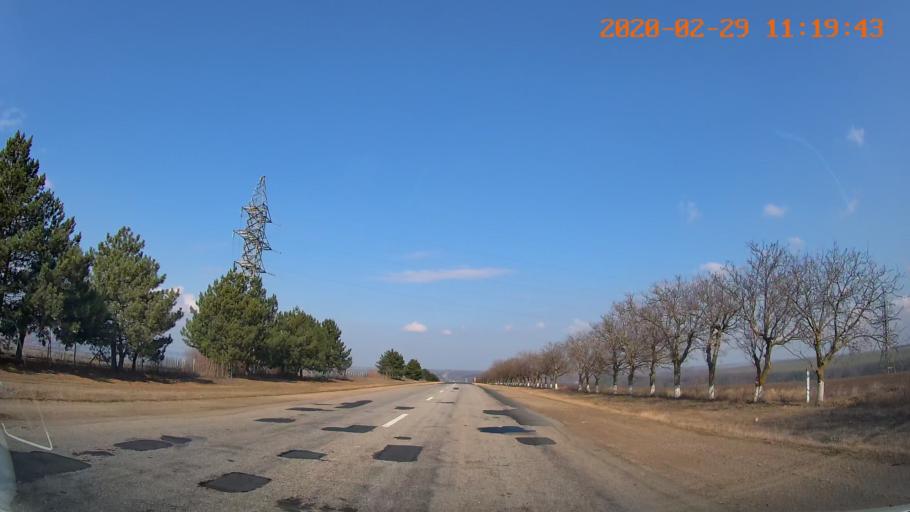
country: MD
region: Telenesti
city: Cocieri
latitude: 47.3542
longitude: 29.1737
